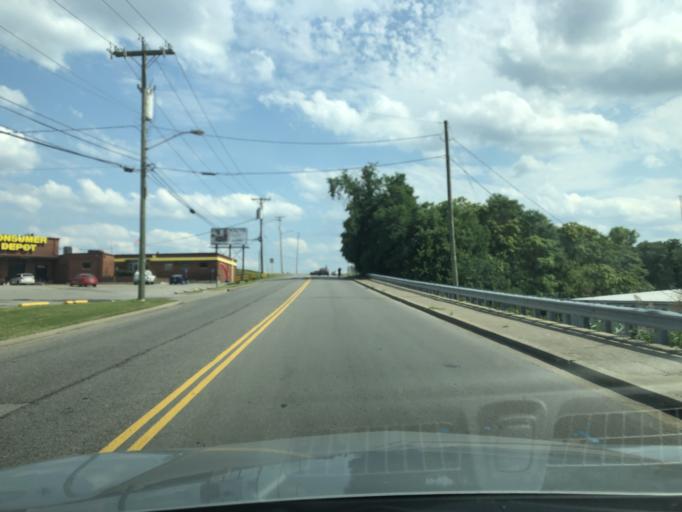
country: US
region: Tennessee
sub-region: Davidson County
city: Oak Hill
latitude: 36.0959
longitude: -86.7589
